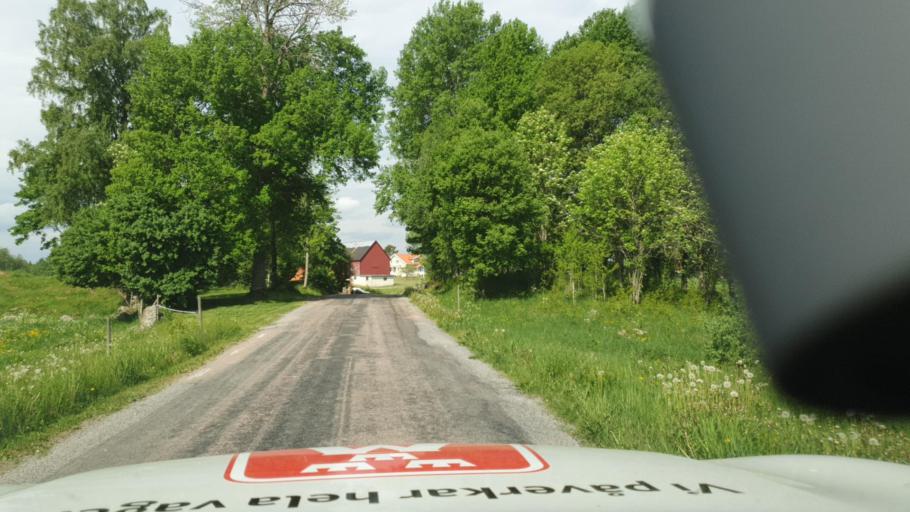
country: SE
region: Vaestra Goetaland
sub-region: Falkopings Kommun
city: Falkoeping
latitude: 57.9877
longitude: 13.4798
